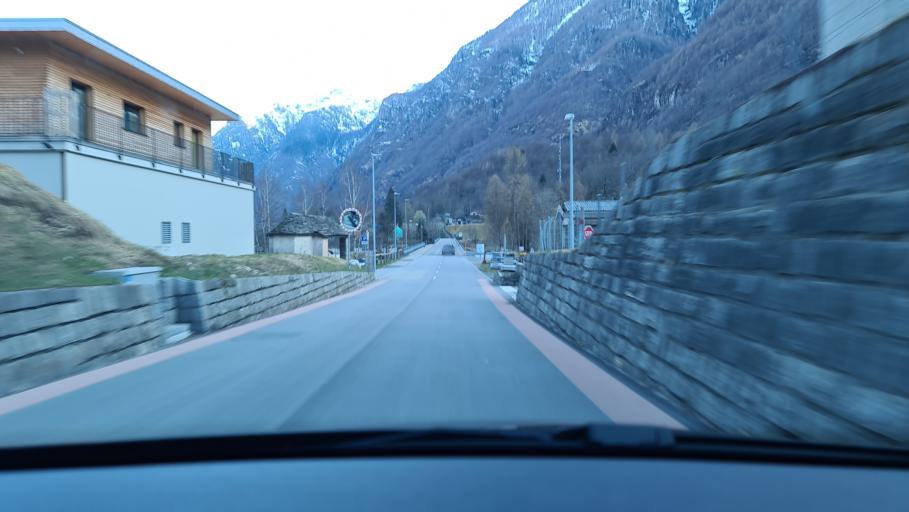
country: CH
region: Ticino
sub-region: Locarno District
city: Lavertezzo
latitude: 46.2950
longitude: 8.7925
